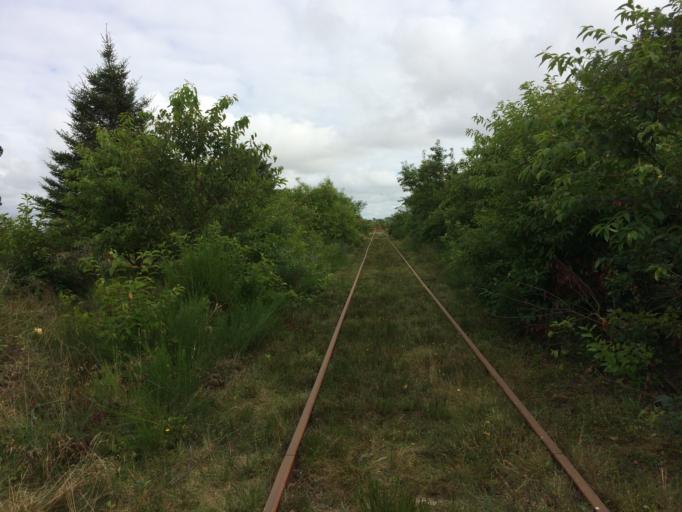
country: DK
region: South Denmark
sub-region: Varde Kommune
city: Oksbol
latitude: 55.8077
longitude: 8.2121
